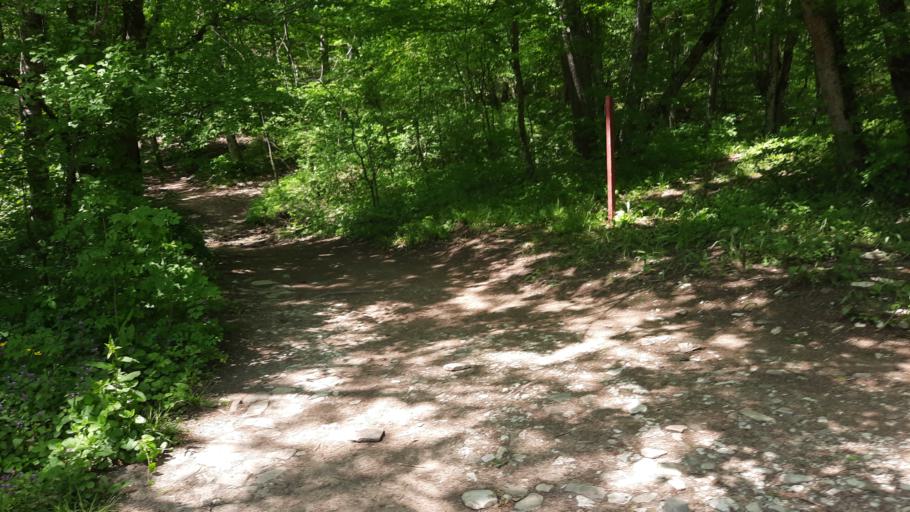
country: RU
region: Krasnodarskiy
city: Divnomorskoye
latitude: 44.5597
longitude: 38.2545
